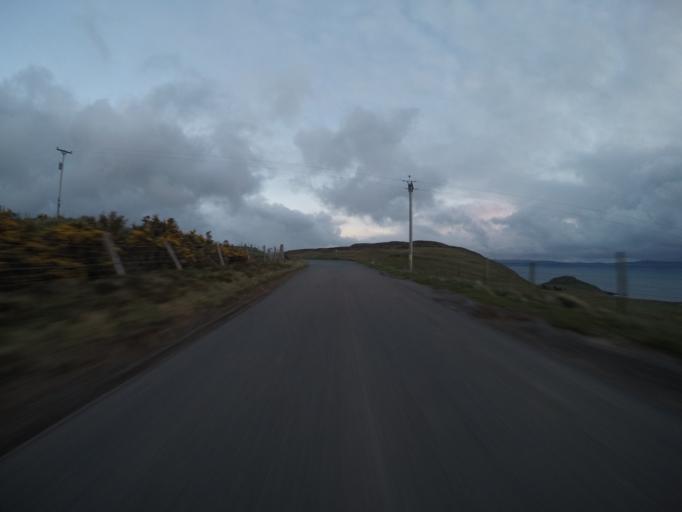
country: GB
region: Scotland
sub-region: Highland
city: Portree
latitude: 57.6026
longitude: -6.3777
